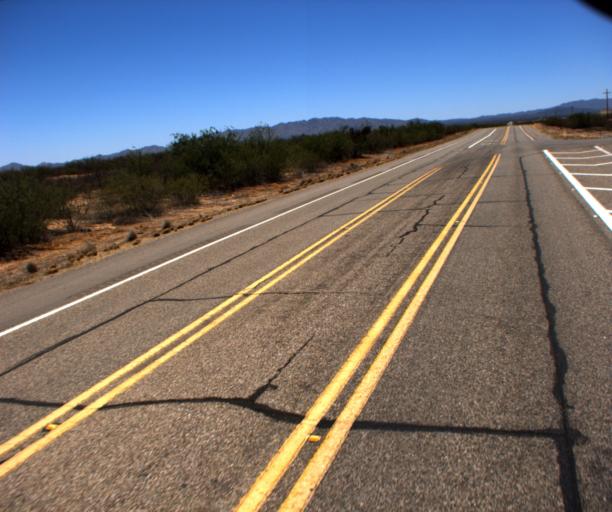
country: US
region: Arizona
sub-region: Pima County
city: Ajo
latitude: 32.1893
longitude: -112.4045
